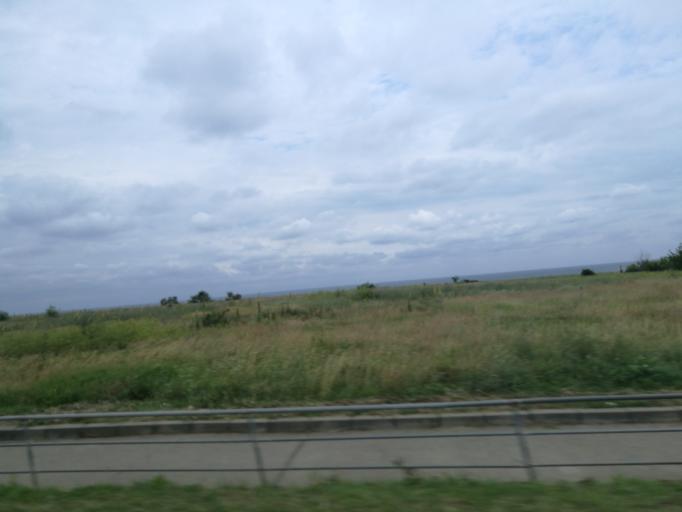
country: RO
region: Constanta
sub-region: Municipiul Mangalia
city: Mangalia
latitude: 43.7746
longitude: 28.5773
